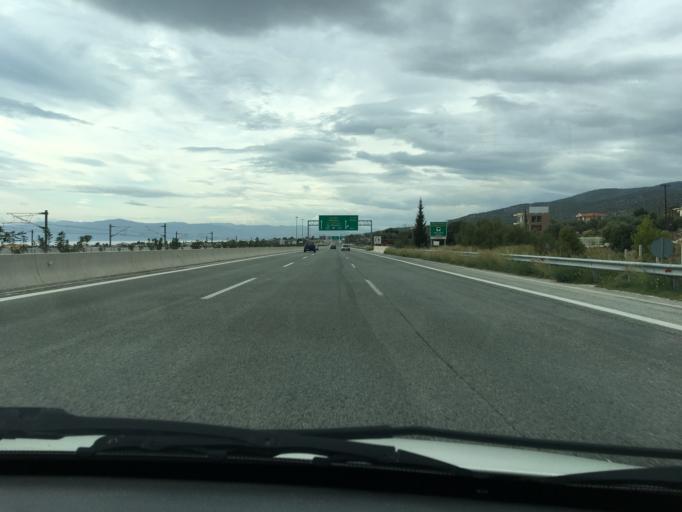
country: GR
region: Attica
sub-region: Nomarchia Dytikis Attikis
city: Kineta
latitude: 37.9708
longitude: 23.2094
